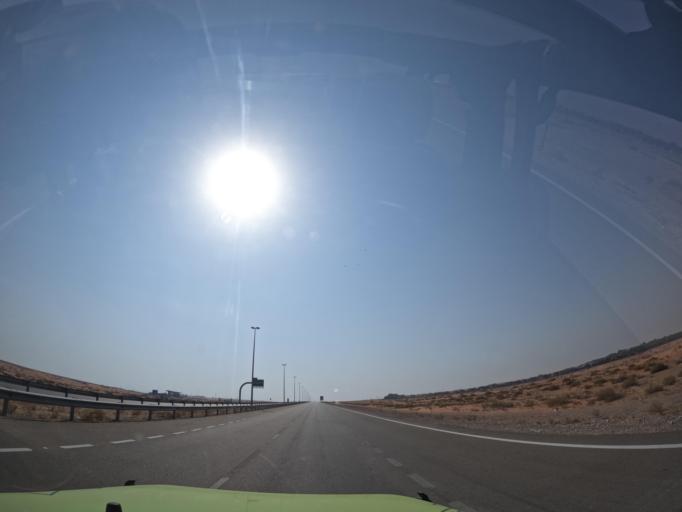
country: OM
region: Al Buraimi
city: Al Buraymi
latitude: 24.4041
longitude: 55.7098
